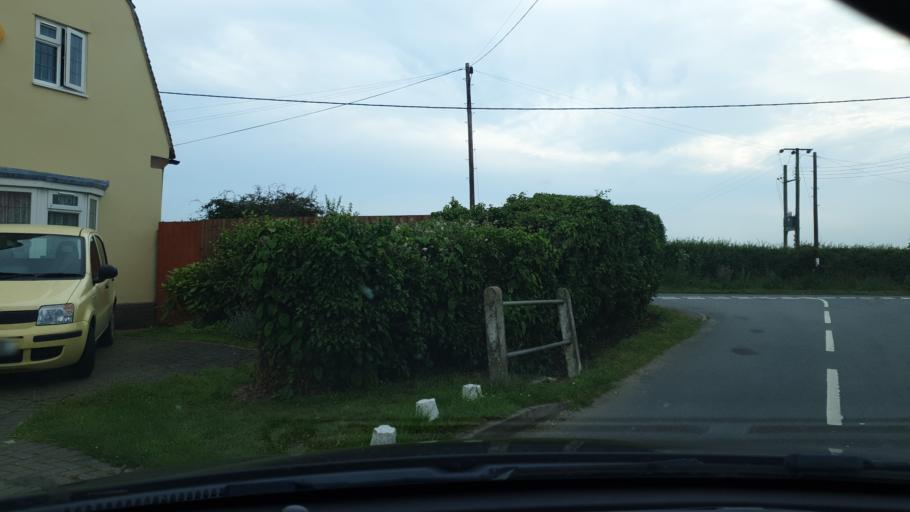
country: GB
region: England
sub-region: Essex
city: Mistley
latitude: 51.8913
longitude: 1.1082
